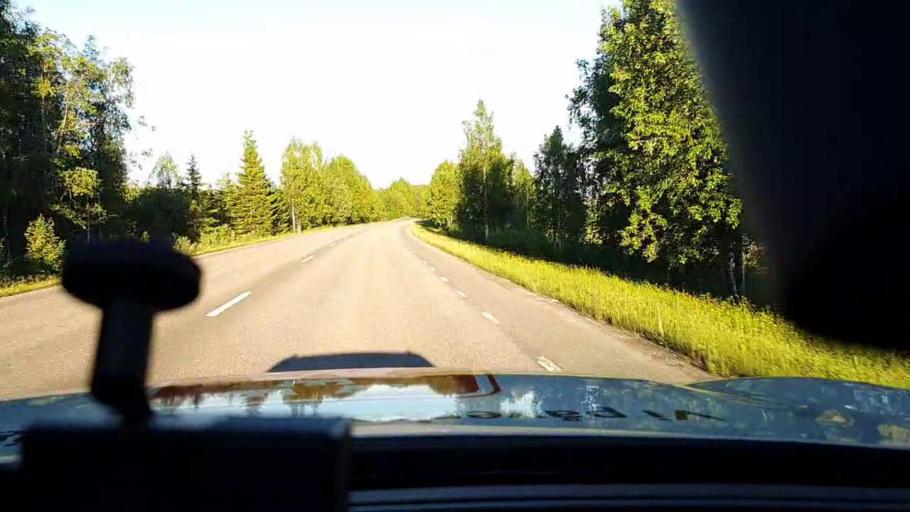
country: SE
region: Norrbotten
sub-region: Lulea Kommun
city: Lulea
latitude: 65.6132
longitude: 22.1580
